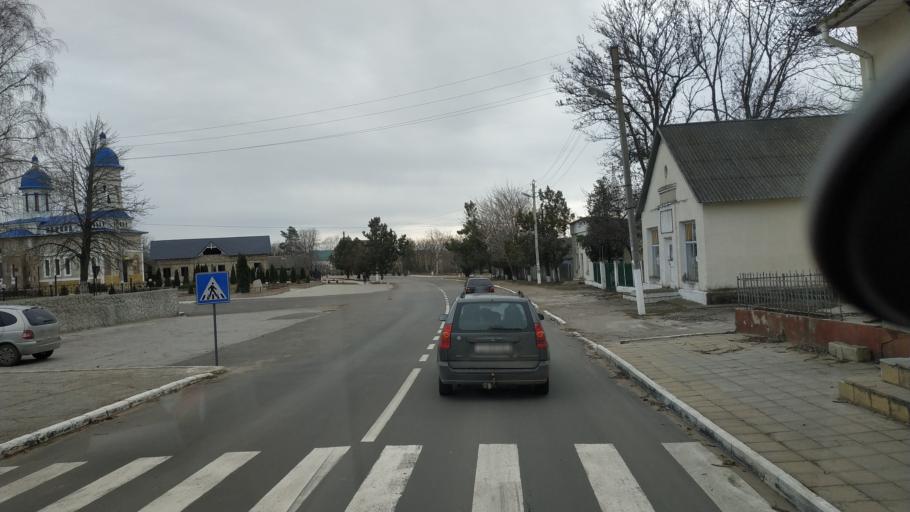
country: MD
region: Telenesti
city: Cocieri
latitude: 47.3093
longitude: 29.1080
